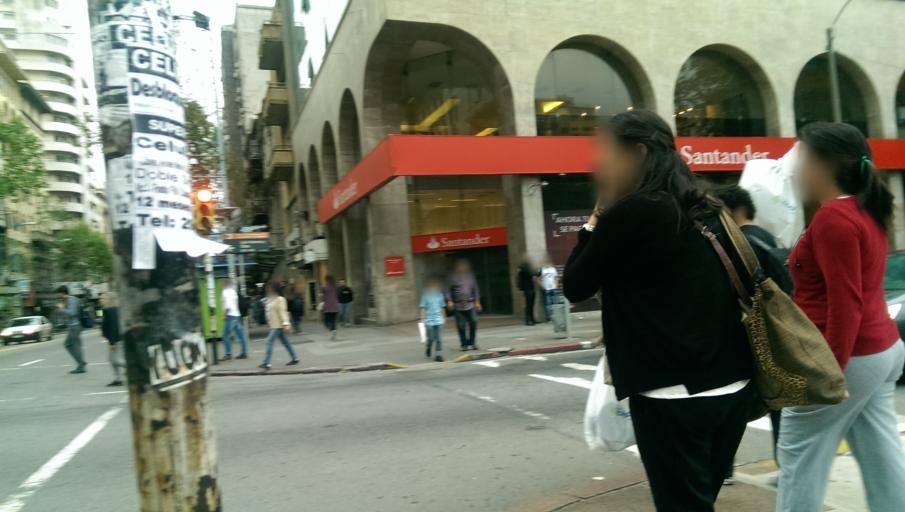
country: UY
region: Montevideo
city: Montevideo
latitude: -34.9061
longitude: -56.1947
